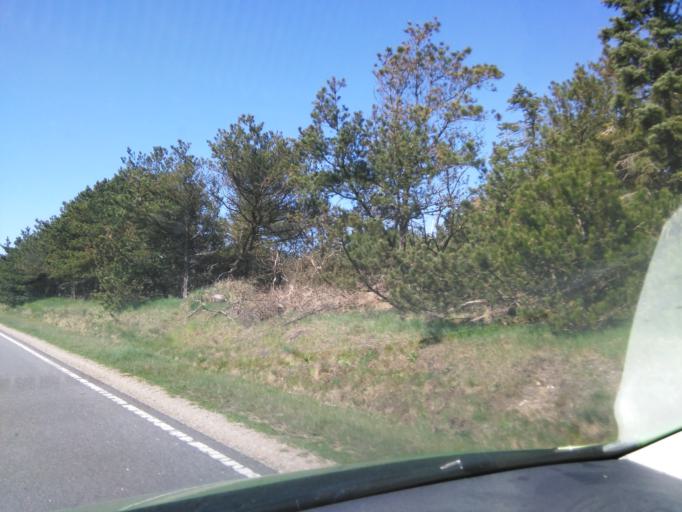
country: DK
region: South Denmark
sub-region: Varde Kommune
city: Varde
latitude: 55.6276
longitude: 8.4093
